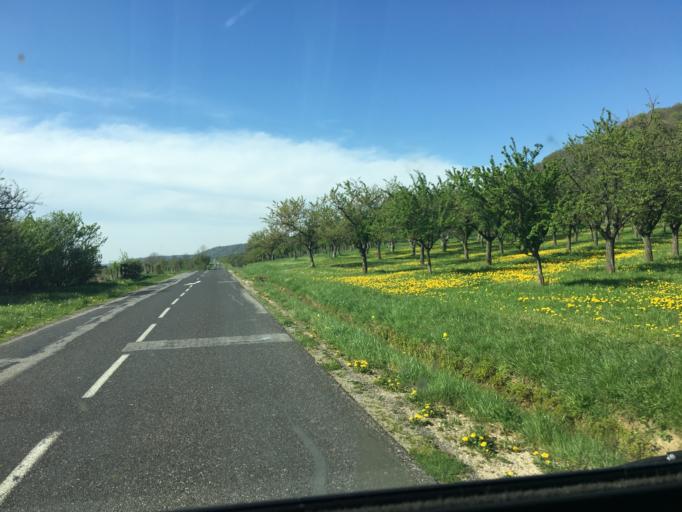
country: FR
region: Lorraine
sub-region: Departement de la Meuse
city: Vigneulles-les-Hattonchatel
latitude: 48.9256
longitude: 5.6879
